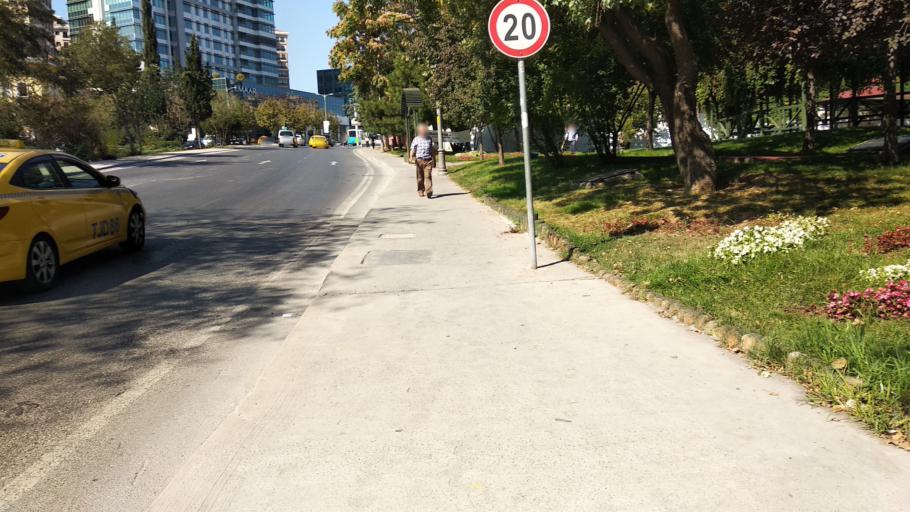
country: TR
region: Istanbul
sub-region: Atasehir
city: Atasehir
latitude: 41.0012
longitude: 29.0734
